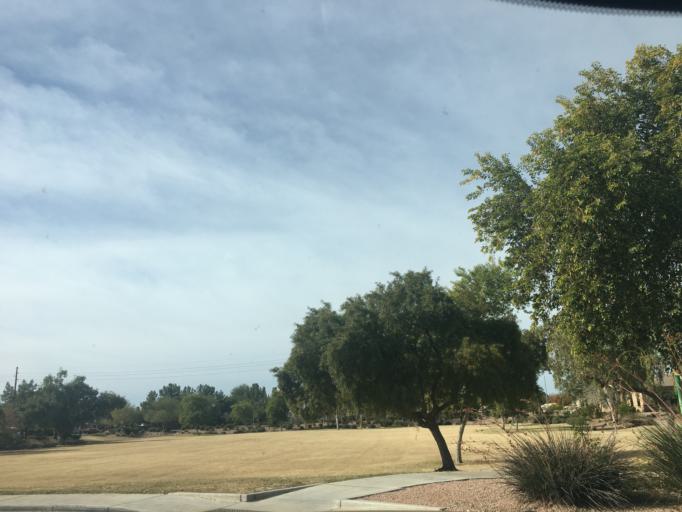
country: US
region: Arizona
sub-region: Maricopa County
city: Gilbert
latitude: 33.3484
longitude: -111.8051
